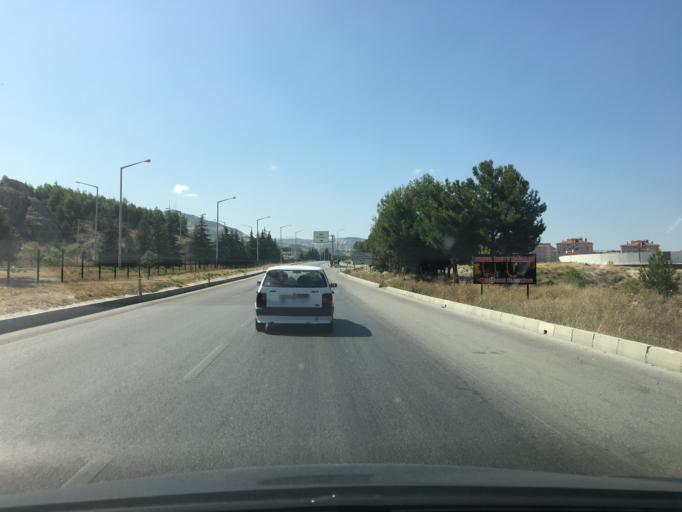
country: TR
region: Burdur
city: Burdur
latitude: 37.7399
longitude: 30.3122
